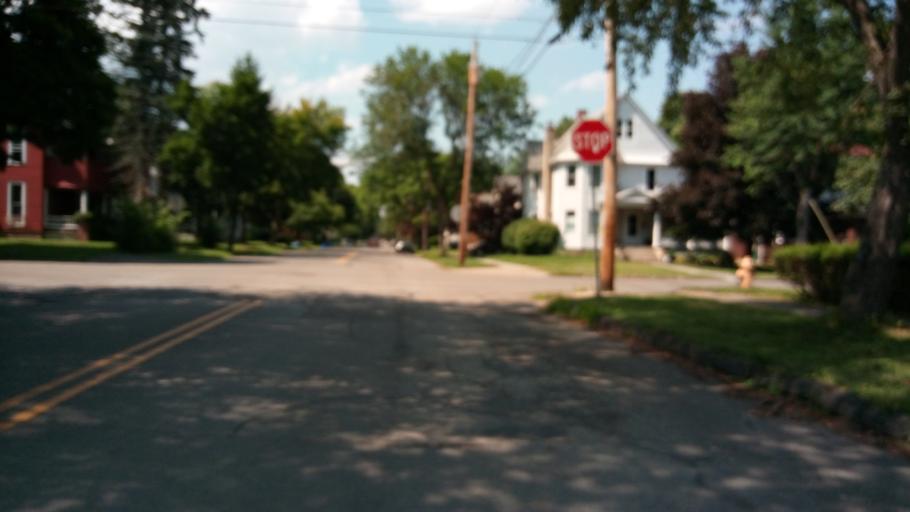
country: US
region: New York
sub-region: Chemung County
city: Elmira
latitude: 42.0902
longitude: -76.8218
